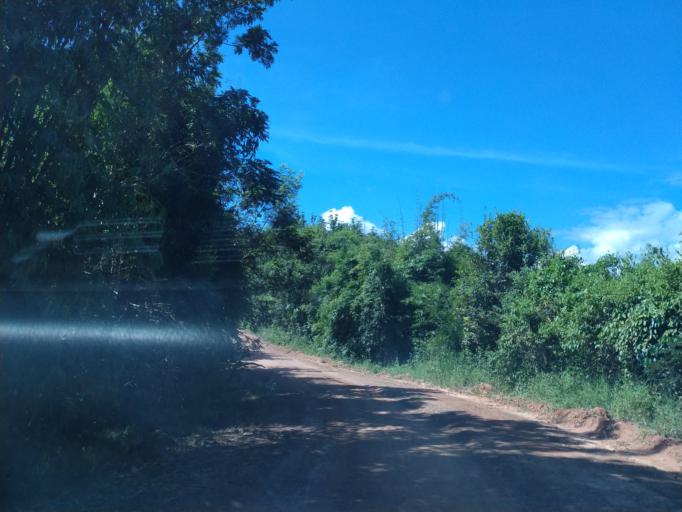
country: LA
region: Vientiane
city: Muang Phon-Hong
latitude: 18.6220
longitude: 102.8726
